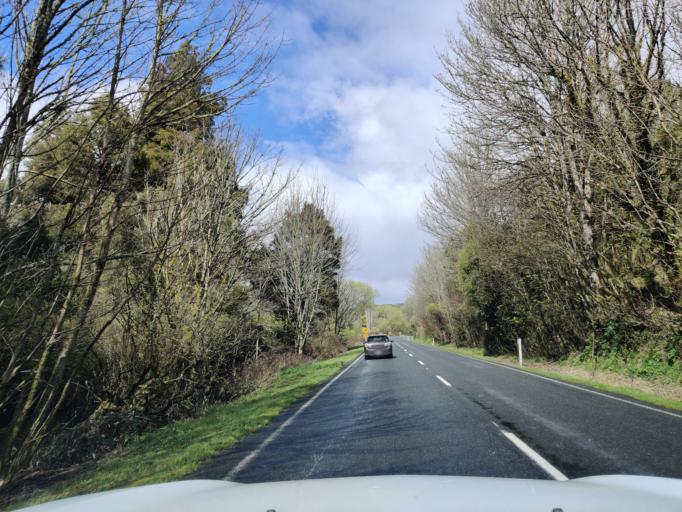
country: NZ
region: Waikato
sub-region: Otorohanga District
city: Otorohanga
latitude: -38.5952
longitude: 175.2193
